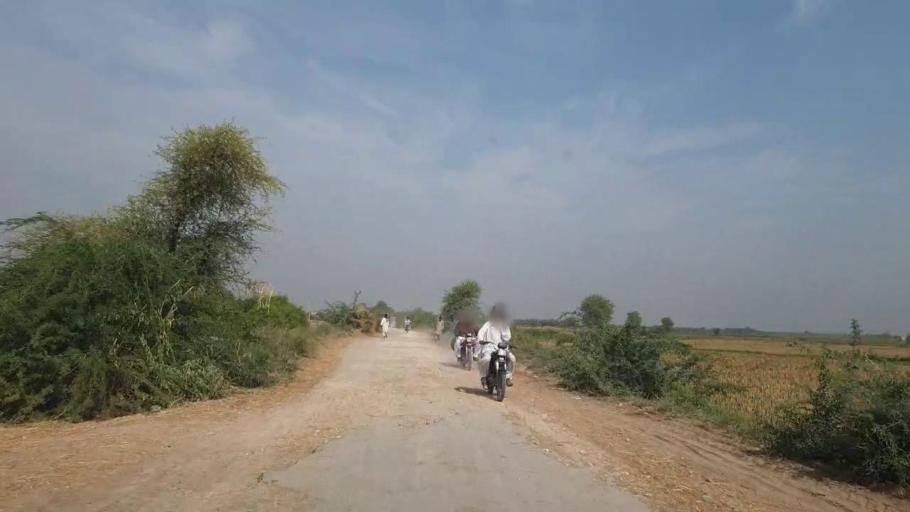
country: PK
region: Sindh
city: Tando Bago
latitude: 24.9085
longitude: 68.9965
